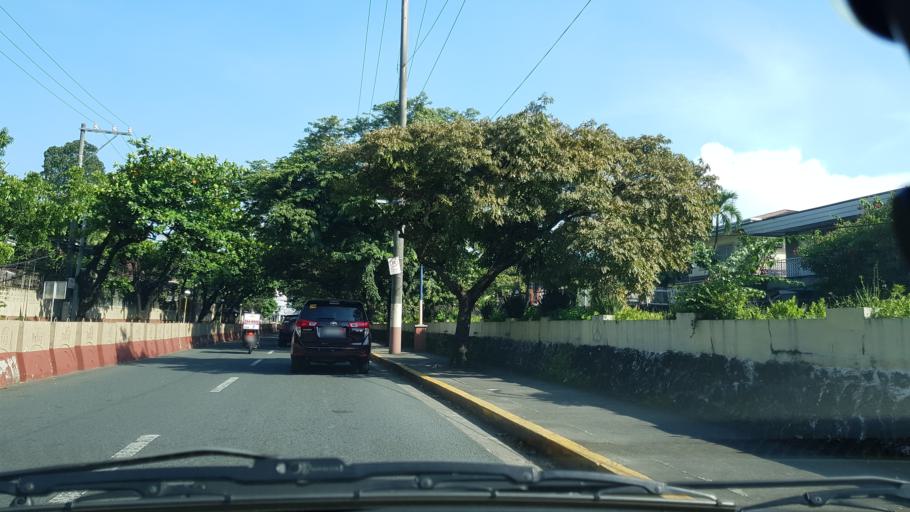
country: PH
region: Metro Manila
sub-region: Pasig
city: Pasig City
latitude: 14.5792
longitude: 121.0714
